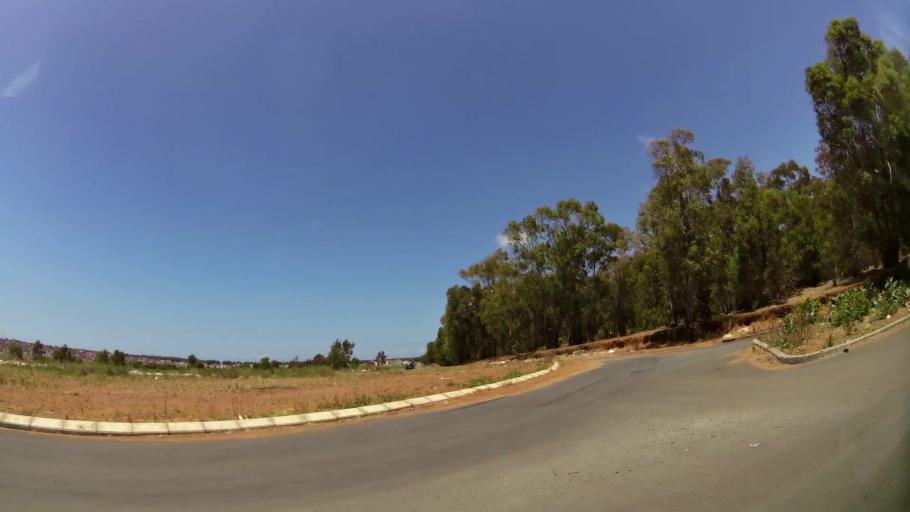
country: MA
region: Gharb-Chrarda-Beni Hssen
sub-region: Kenitra Province
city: Kenitra
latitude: 34.2572
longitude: -6.6290
